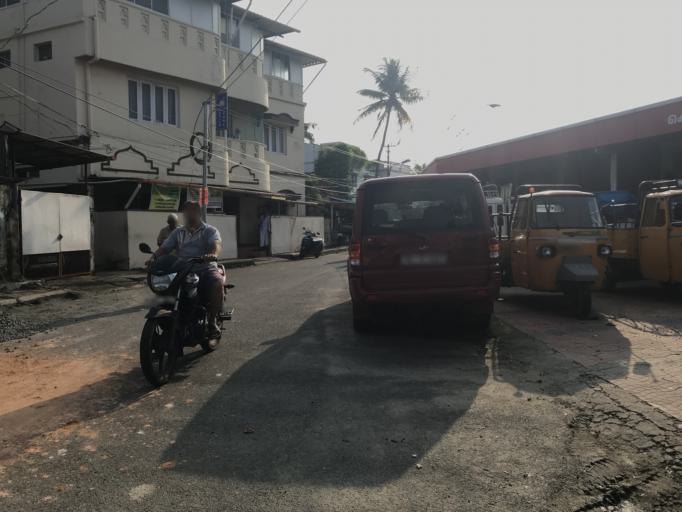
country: IN
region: Kerala
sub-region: Ernakulam
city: Cochin
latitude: 9.9665
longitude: 76.2490
